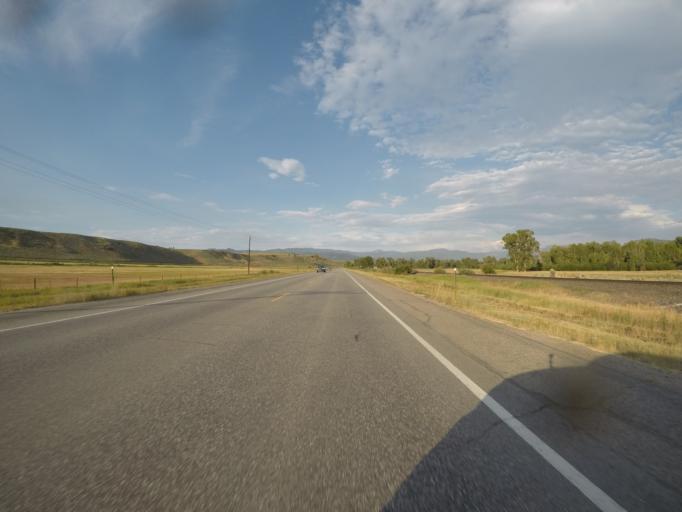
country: US
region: Colorado
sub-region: Routt County
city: Steamboat Springs
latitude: 40.4956
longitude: -106.9442
